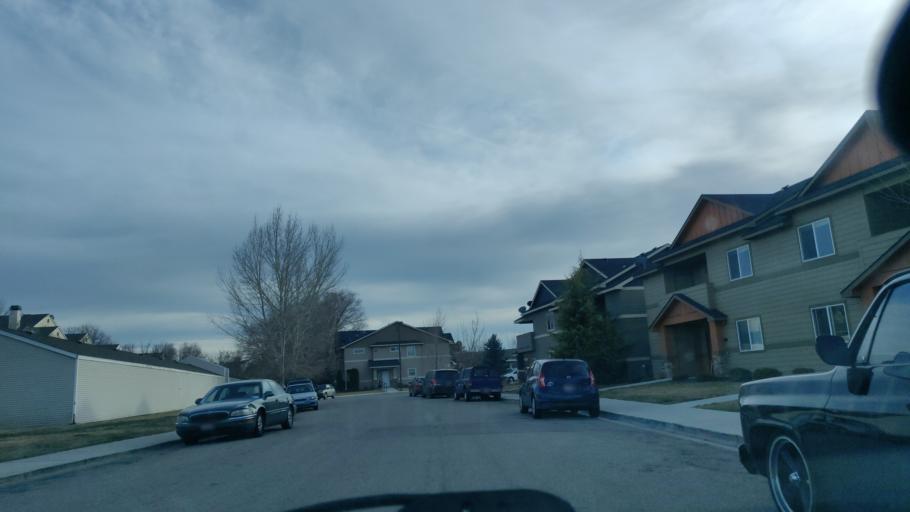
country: US
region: Idaho
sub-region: Ada County
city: Garden City
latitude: 43.6167
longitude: -116.2638
